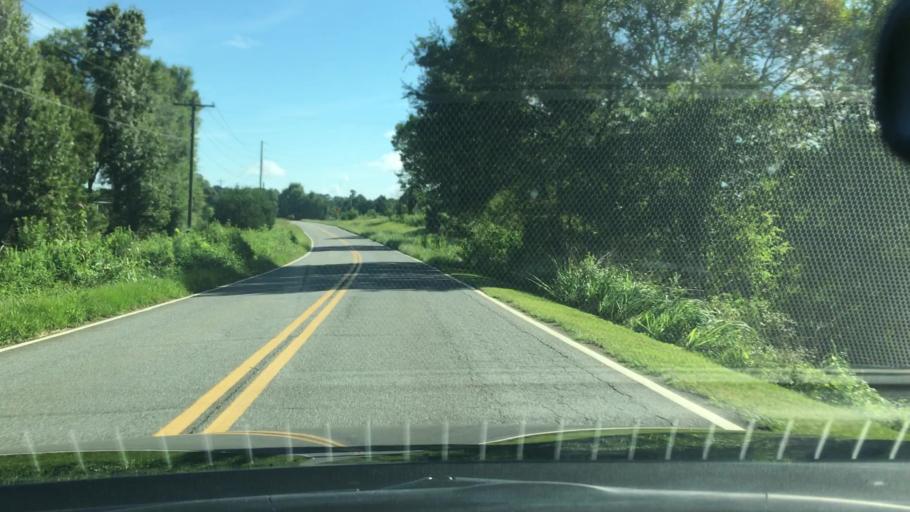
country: US
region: Georgia
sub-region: Putnam County
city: Jefferson
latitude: 33.4416
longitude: -83.3290
